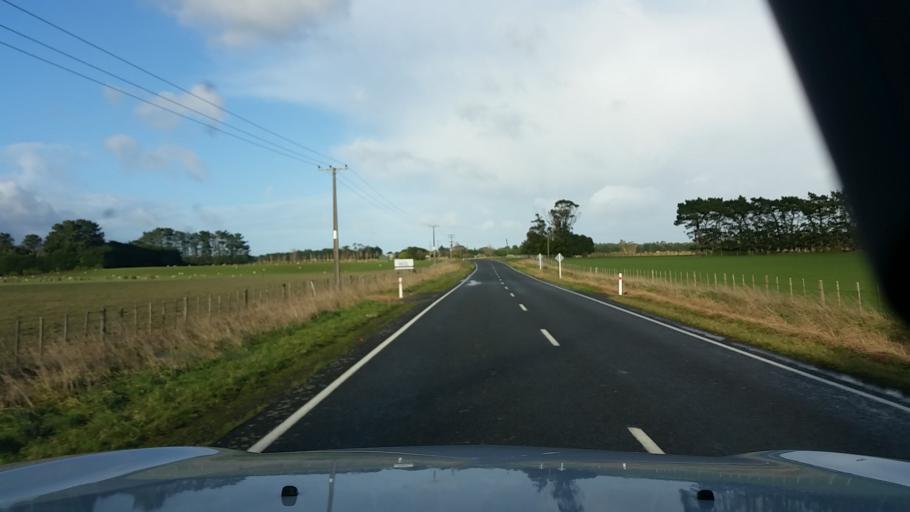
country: NZ
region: Wellington
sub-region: Upper Hutt City
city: Upper Hutt
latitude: -41.3451
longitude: 175.2087
